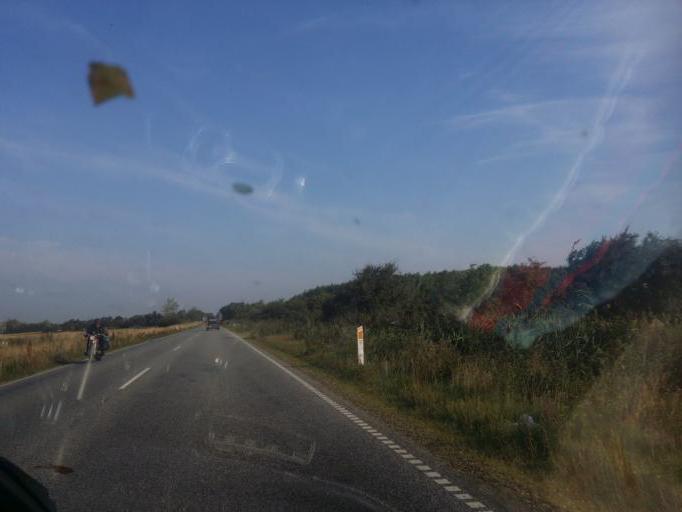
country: DK
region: South Denmark
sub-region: Tonder Kommune
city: Sherrebek
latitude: 55.1439
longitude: 8.7883
